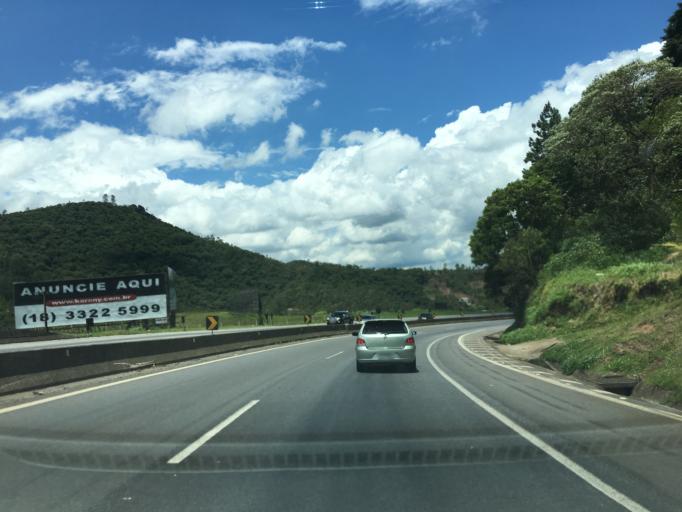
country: BR
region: Sao Paulo
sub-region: Mairipora
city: Mairipora
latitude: -23.2892
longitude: -46.5832
